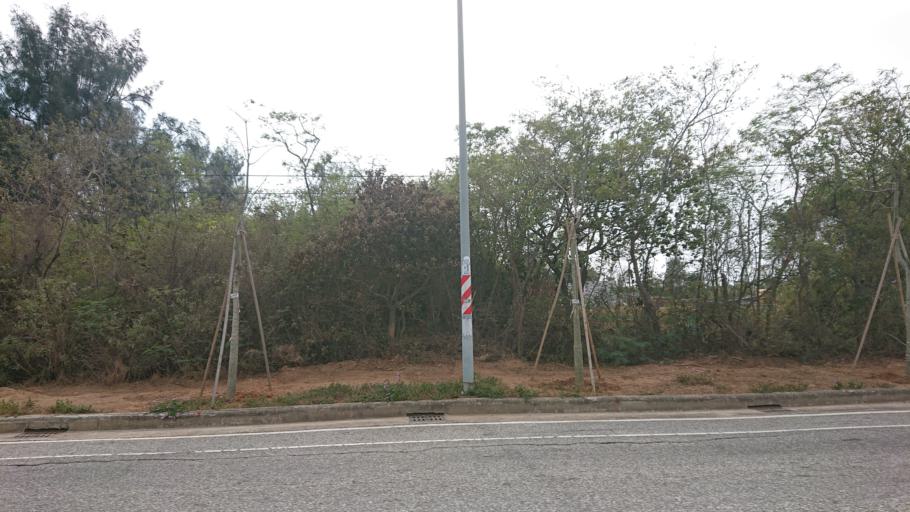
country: TW
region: Fukien
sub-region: Kinmen
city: Jincheng
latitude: 24.4559
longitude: 118.3775
